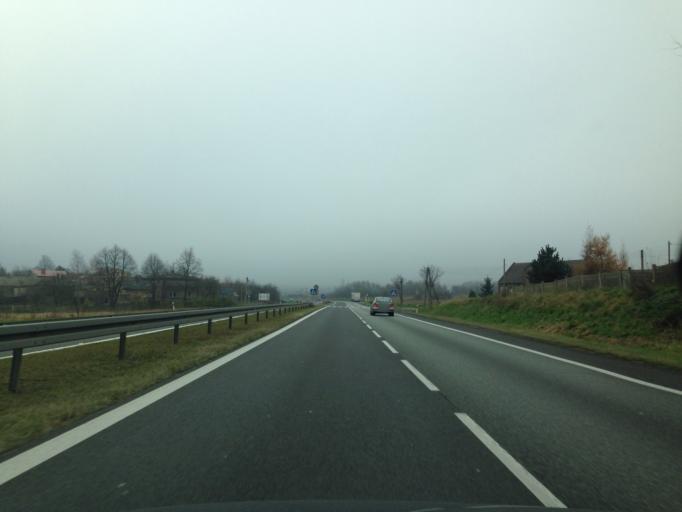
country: PL
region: Silesian Voivodeship
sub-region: Powiat myszkowski
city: Kozieglowy
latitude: 50.5721
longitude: 19.1652
